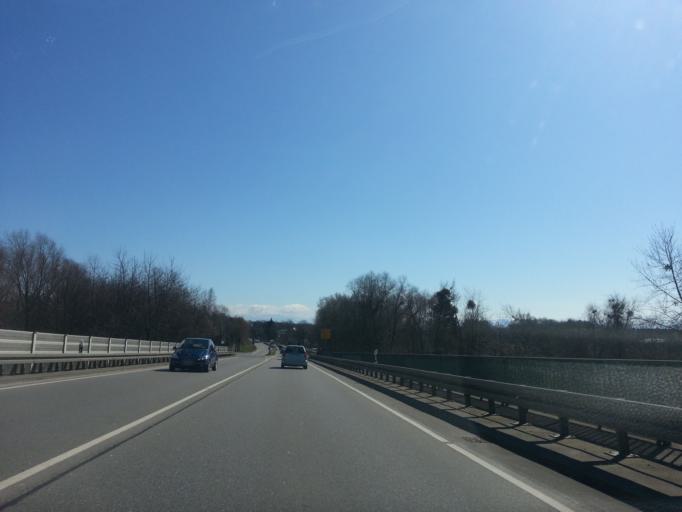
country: DE
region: Baden-Wuerttemberg
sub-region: Tuebingen Region
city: Friedrichshafen
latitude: 47.6595
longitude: 9.4977
